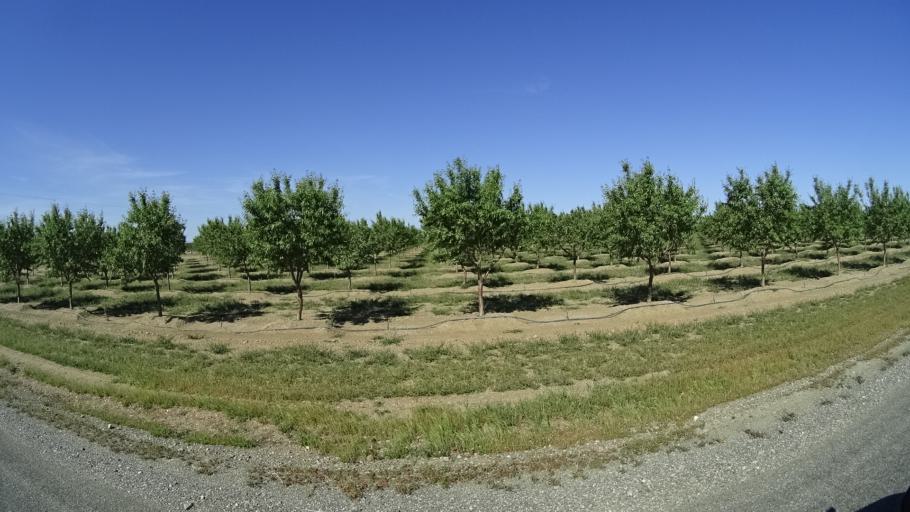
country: US
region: California
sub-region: Glenn County
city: Willows
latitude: 39.6189
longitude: -122.1564
